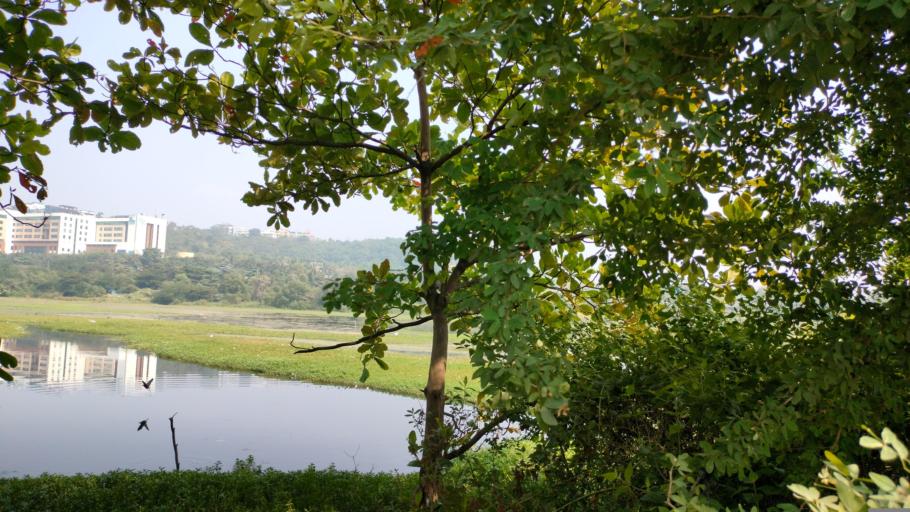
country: IN
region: Maharashtra
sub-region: Thane
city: Navi Mumbai
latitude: 19.0175
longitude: 73.0258
